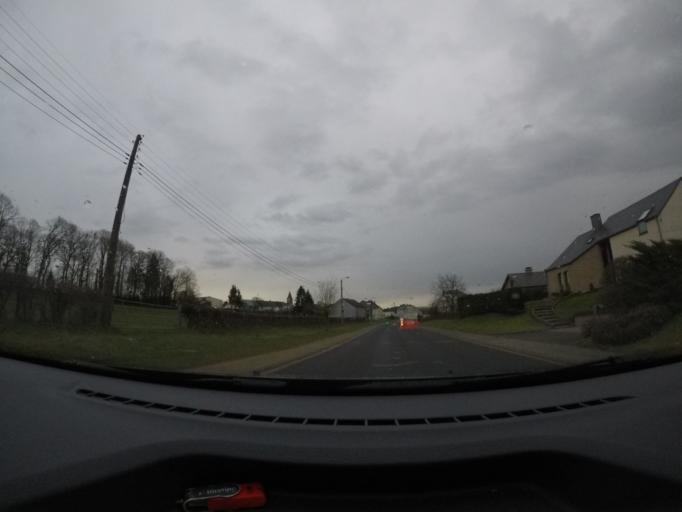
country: BE
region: Wallonia
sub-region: Province du Luxembourg
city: Tintigny
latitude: 49.6686
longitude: 5.4955
